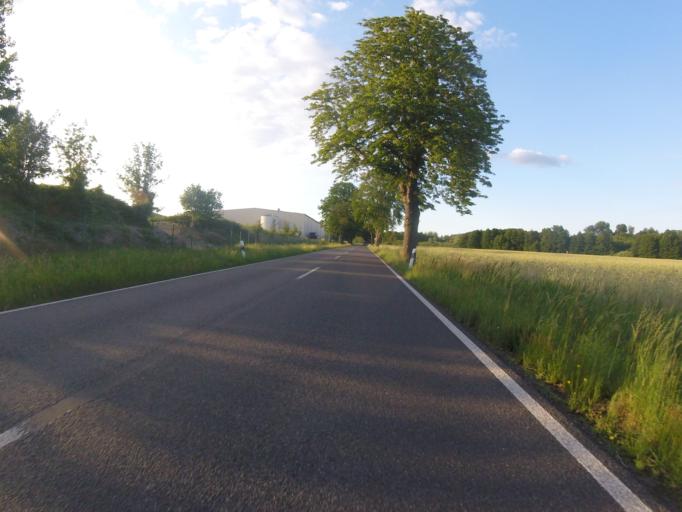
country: DE
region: Brandenburg
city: Mittenwalde
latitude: 52.2320
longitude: 13.5498
